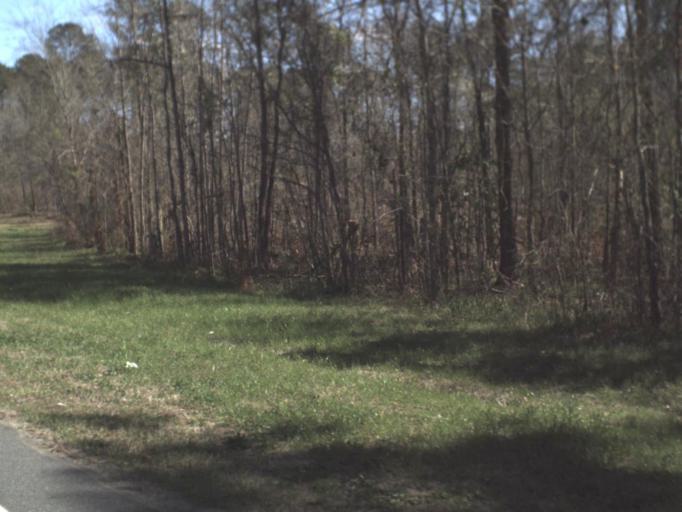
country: US
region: Florida
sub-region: Gadsden County
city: Chattahoochee
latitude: 30.7029
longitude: -84.7914
